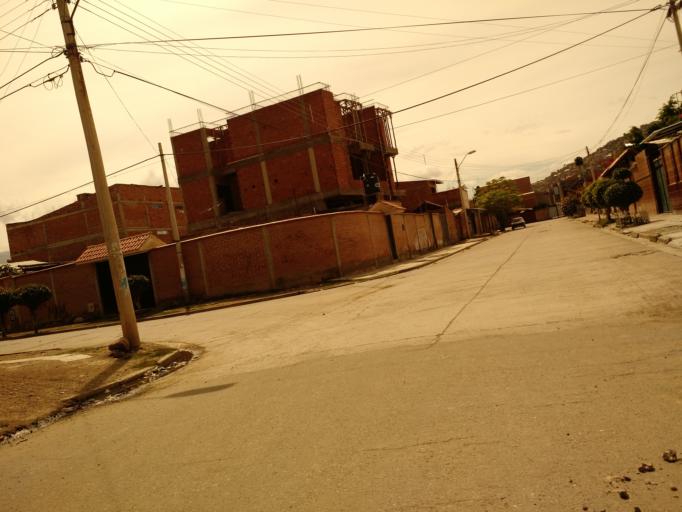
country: BO
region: Cochabamba
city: Cochabamba
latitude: -17.4223
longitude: -66.1631
